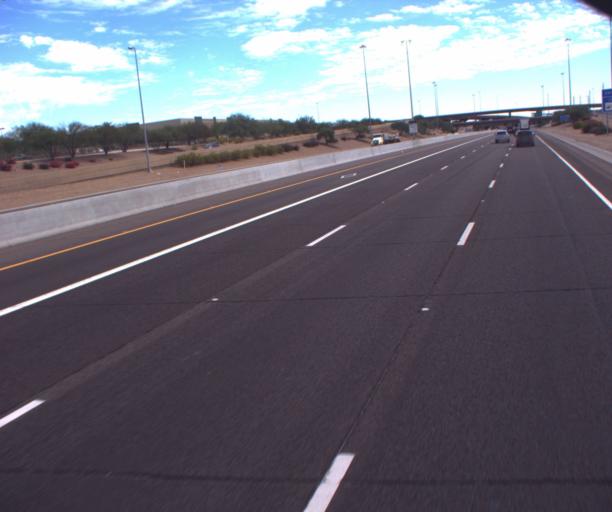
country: US
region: Arizona
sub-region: Maricopa County
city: Chandler
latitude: 33.2918
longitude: -111.9017
